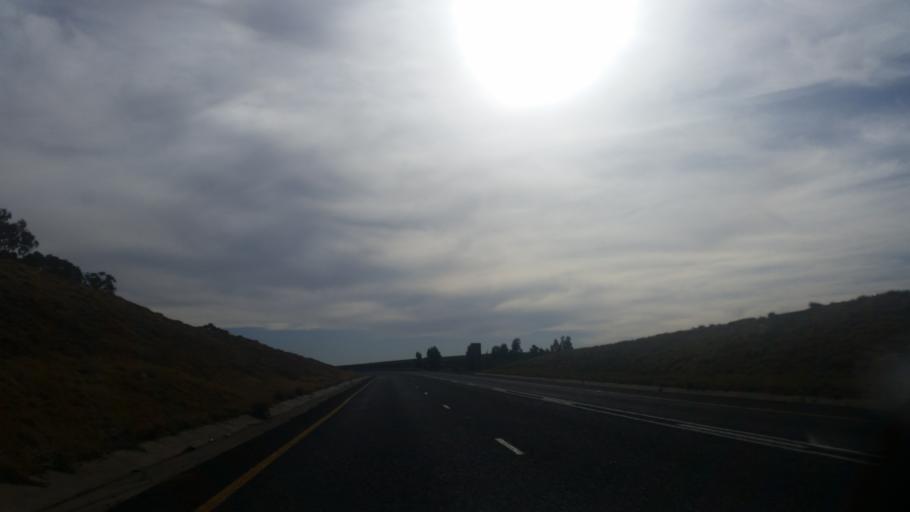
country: ZA
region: Orange Free State
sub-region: Thabo Mofutsanyana District Municipality
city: Phuthaditjhaba
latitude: -28.2716
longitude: 28.8572
